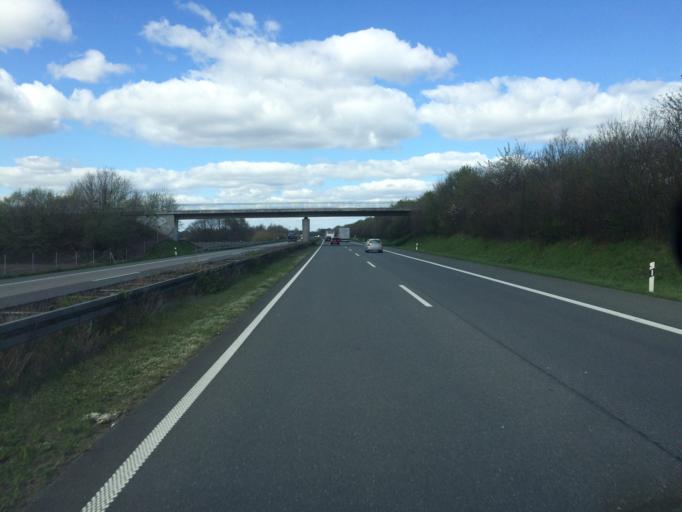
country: DE
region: North Rhine-Westphalia
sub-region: Regierungsbezirk Munster
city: Heek
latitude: 52.1340
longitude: 7.0893
